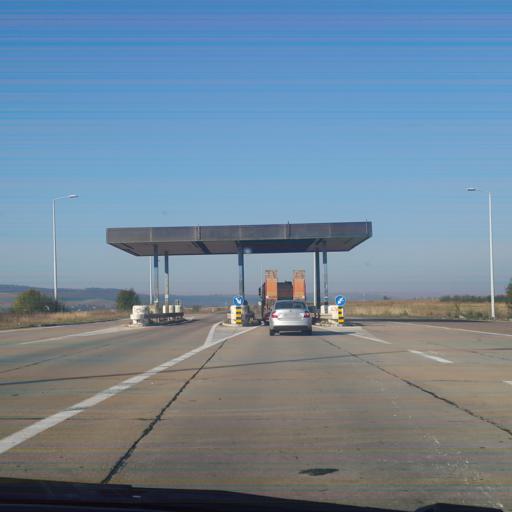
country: RS
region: Central Serbia
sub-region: Nisavski Okrug
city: Merosina
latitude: 43.2795
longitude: 21.7989
